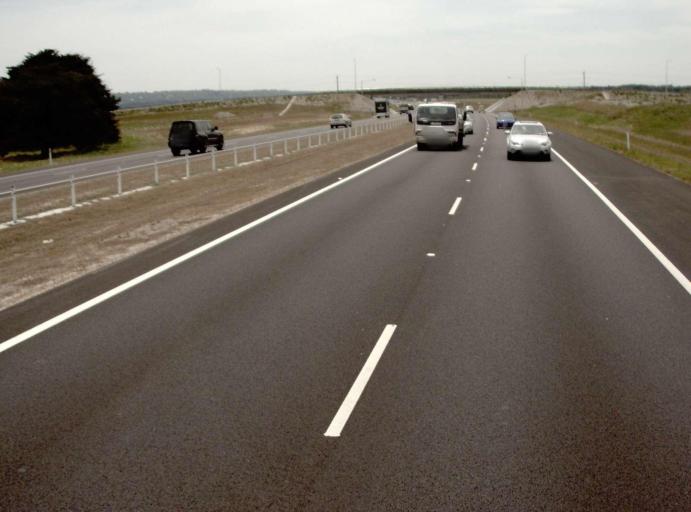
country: AU
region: Victoria
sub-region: Mornington Peninsula
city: Moorooduc
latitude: -38.2547
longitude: 145.1162
